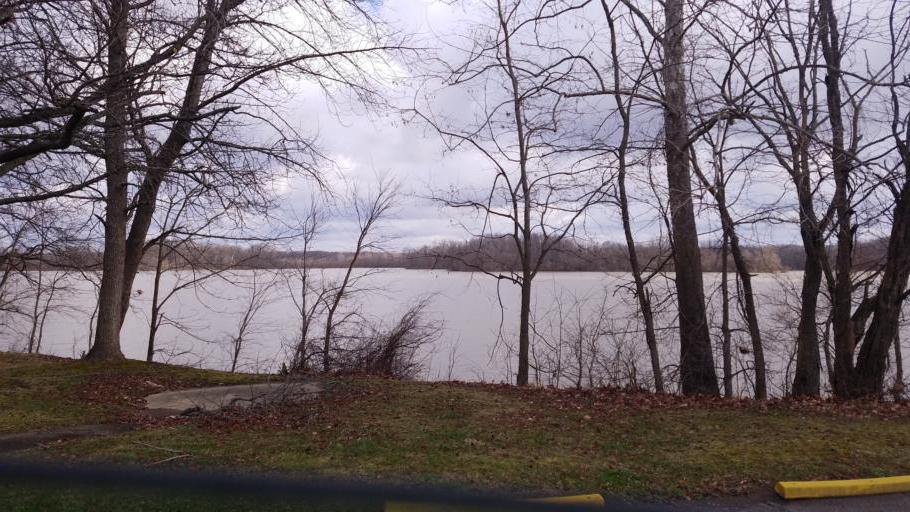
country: US
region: Ohio
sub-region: Knox County
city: Fredericktown
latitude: 40.5056
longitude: -82.5835
